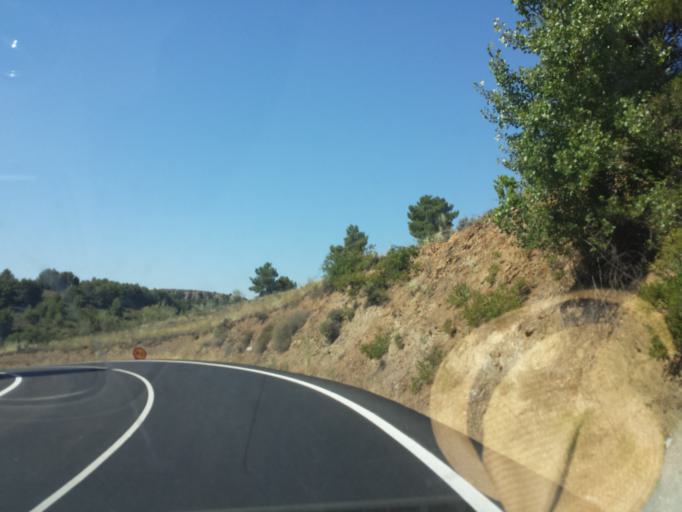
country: ES
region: Aragon
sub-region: Provincia de Zaragoza
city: Munebrega
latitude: 41.2242
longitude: -1.7417
